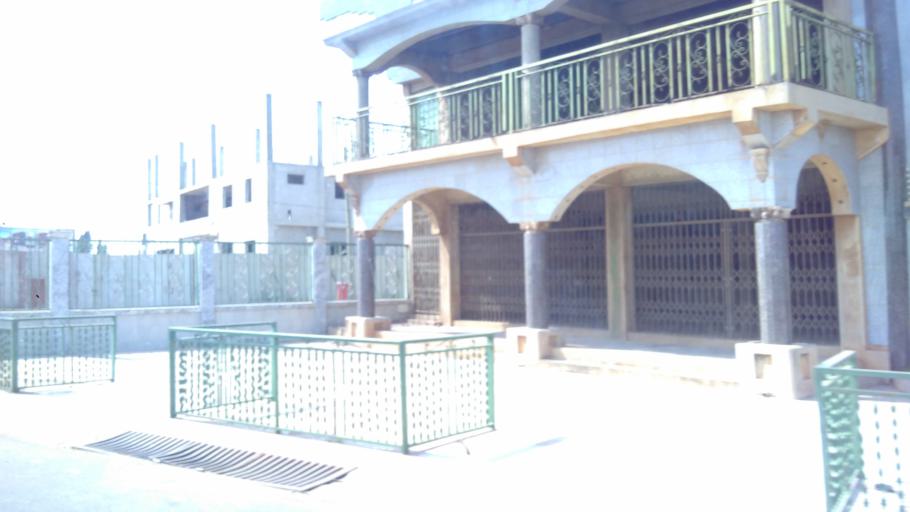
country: GH
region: Greater Accra
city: Nungua
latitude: 5.6145
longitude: -0.0725
